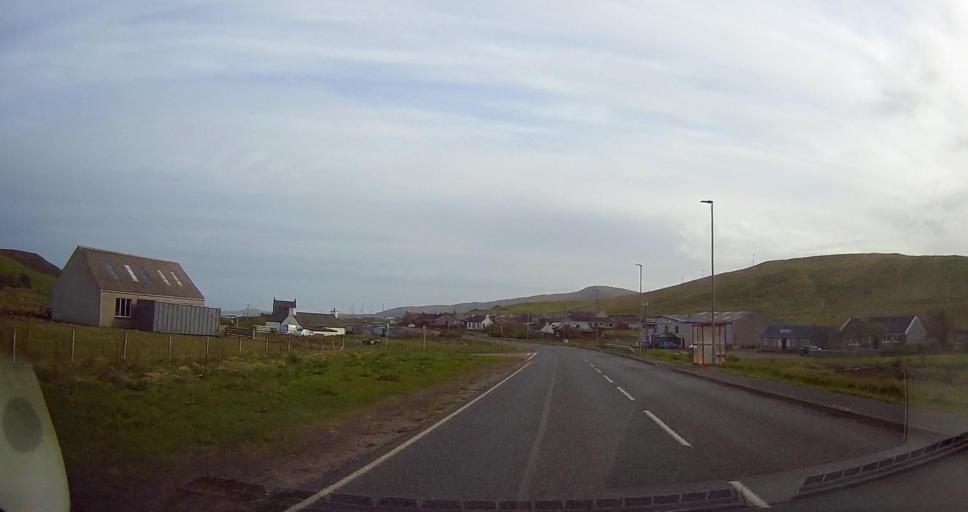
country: GB
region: Scotland
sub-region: Shetland Islands
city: Sandwick
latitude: 60.0568
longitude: -1.2248
